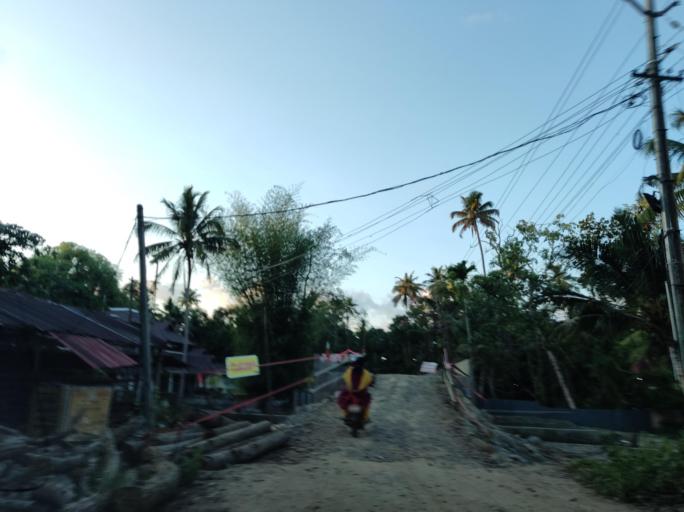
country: IN
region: Kerala
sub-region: Alappuzha
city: Vayalar
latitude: 9.7186
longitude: 76.2967
